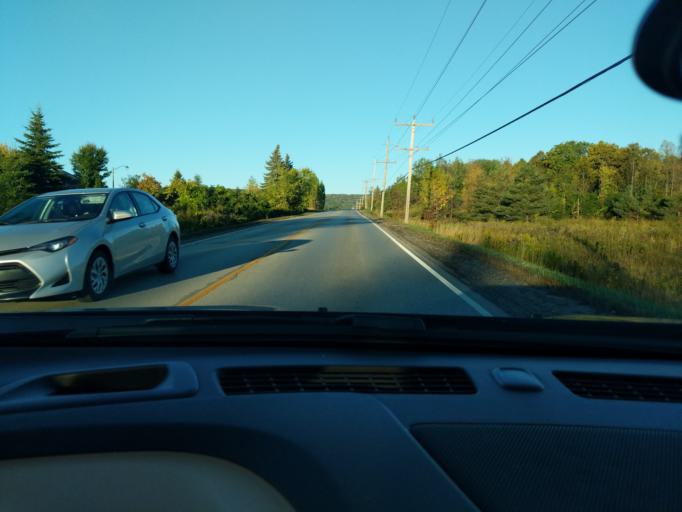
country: CA
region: Ontario
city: Collingwood
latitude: 44.4987
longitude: -80.2583
